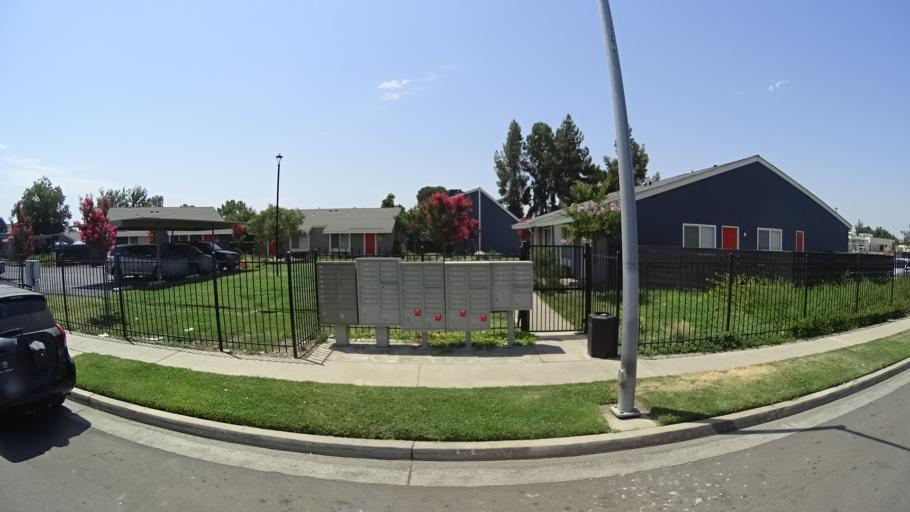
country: US
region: California
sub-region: Fresno County
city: Fresno
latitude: 36.7198
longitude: -119.7969
